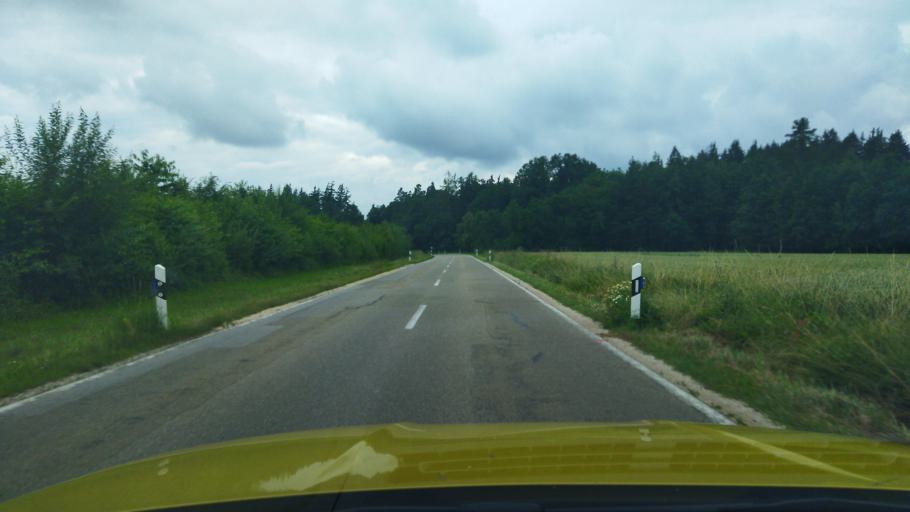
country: DE
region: Bavaria
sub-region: Regierungsbezirk Mittelfranken
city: Hottingen
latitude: 49.0837
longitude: 11.0106
